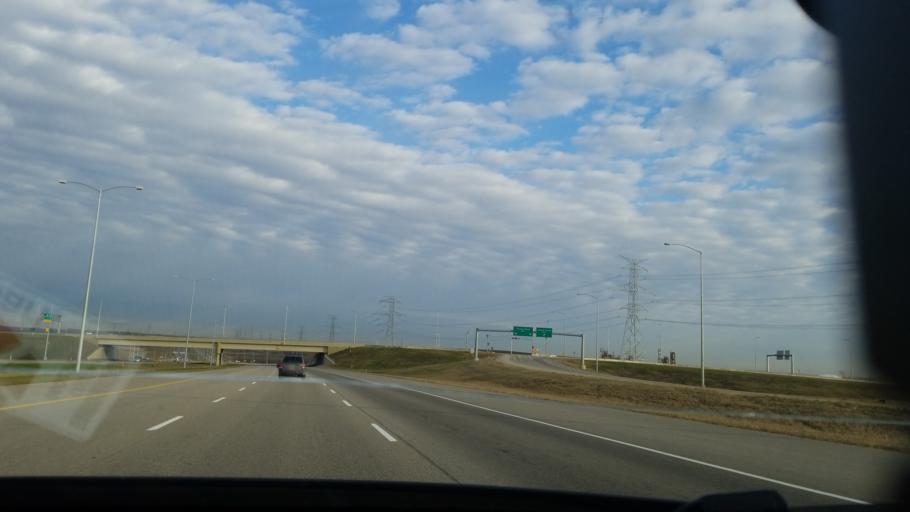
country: CA
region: Alberta
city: Sherwood Park
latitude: 53.5846
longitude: -113.3444
